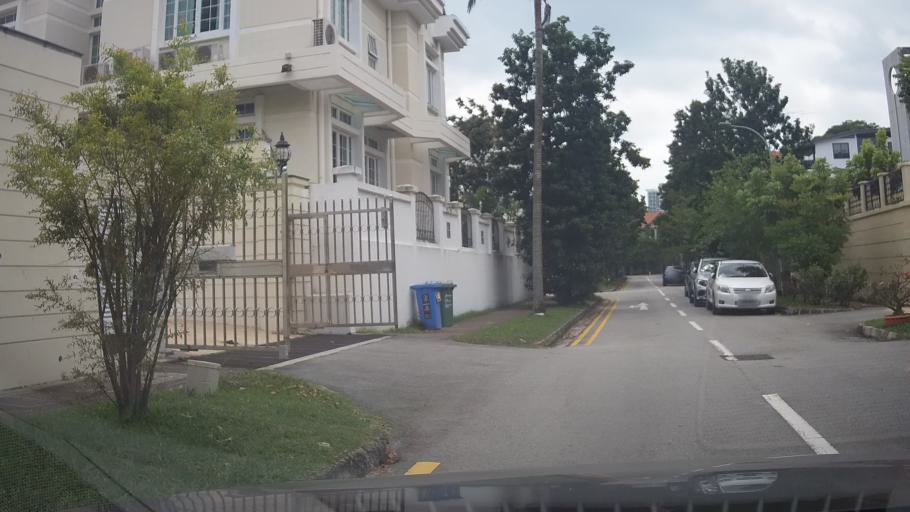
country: SG
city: Singapore
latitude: 1.3053
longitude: 103.8859
